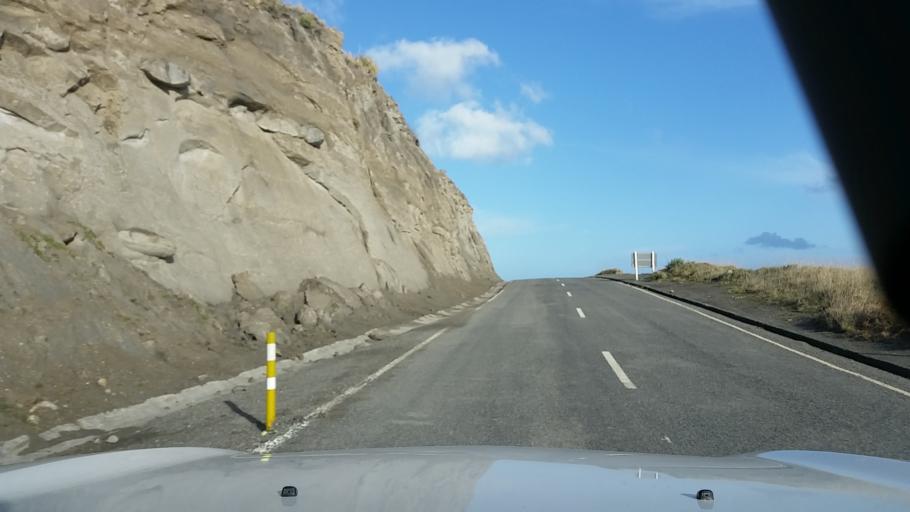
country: NZ
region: Wellington
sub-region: South Wairarapa District
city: Waipawa
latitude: -41.4668
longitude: 175.2141
